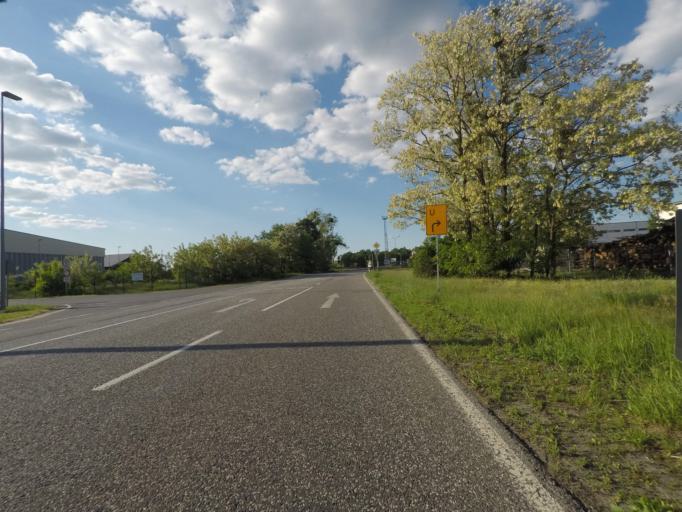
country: DE
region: Brandenburg
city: Eberswalde
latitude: 52.8506
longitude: 13.7902
